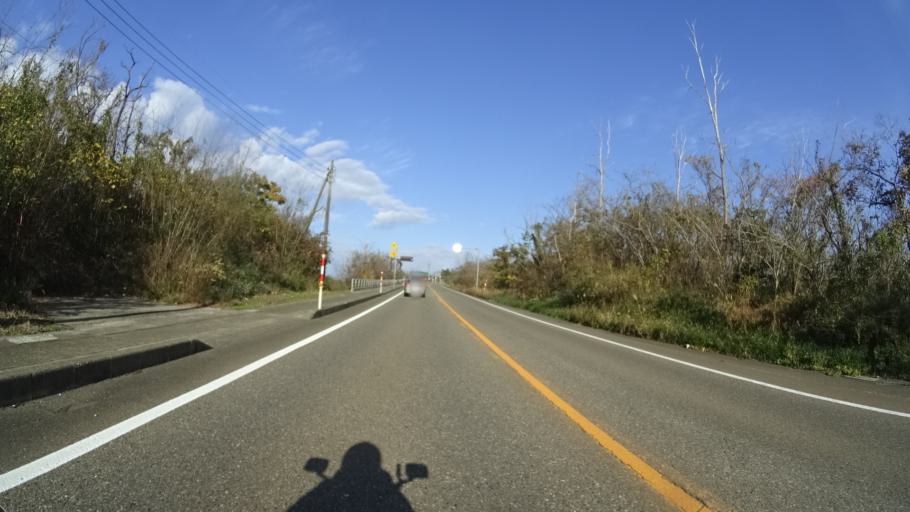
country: JP
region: Niigata
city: Joetsu
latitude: 37.2618
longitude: 138.3719
